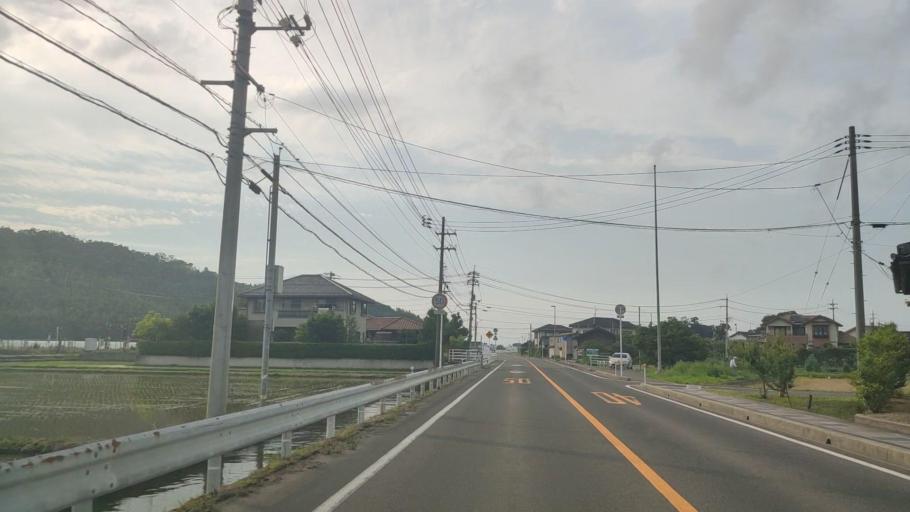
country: JP
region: Tottori
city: Kurayoshi
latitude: 35.4625
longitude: 133.8337
